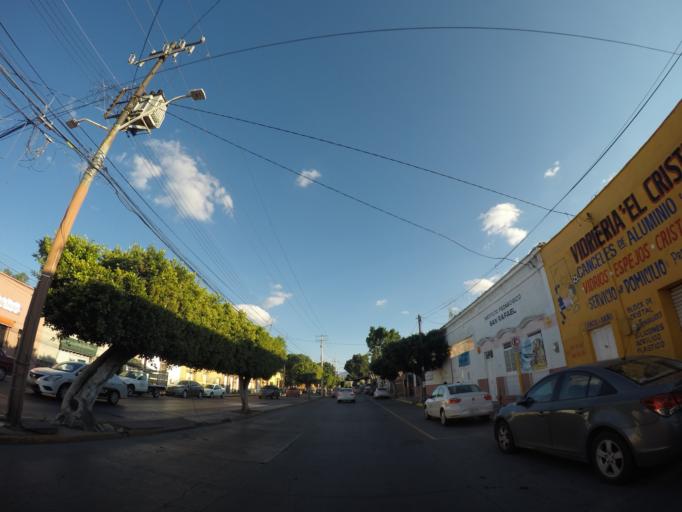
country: MX
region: San Luis Potosi
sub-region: San Luis Potosi
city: San Luis Potosi
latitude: 22.1609
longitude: -100.9800
